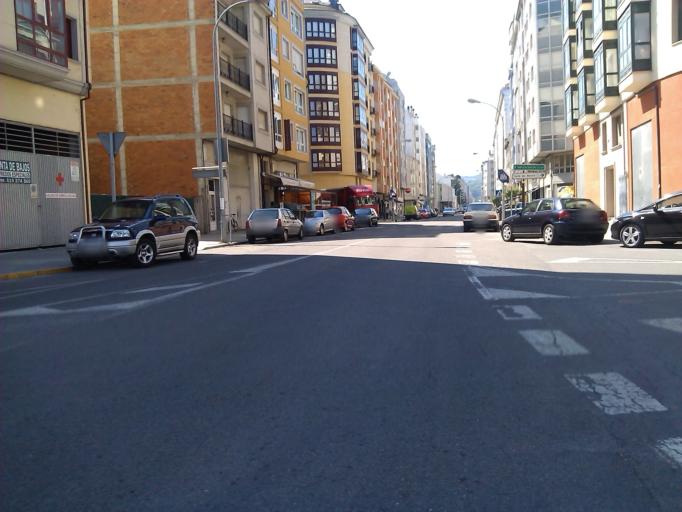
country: ES
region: Galicia
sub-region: Provincia de Lugo
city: Sarria
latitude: 42.7754
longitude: -7.4058
